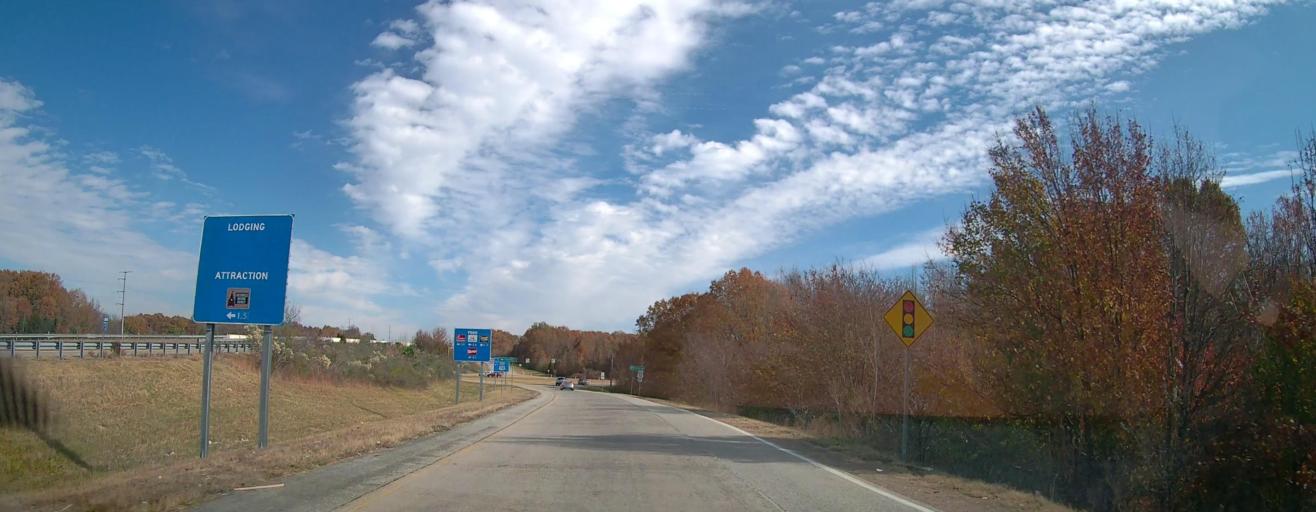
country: US
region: Tennessee
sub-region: Shelby County
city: Collierville
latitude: 35.0213
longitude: -89.6608
